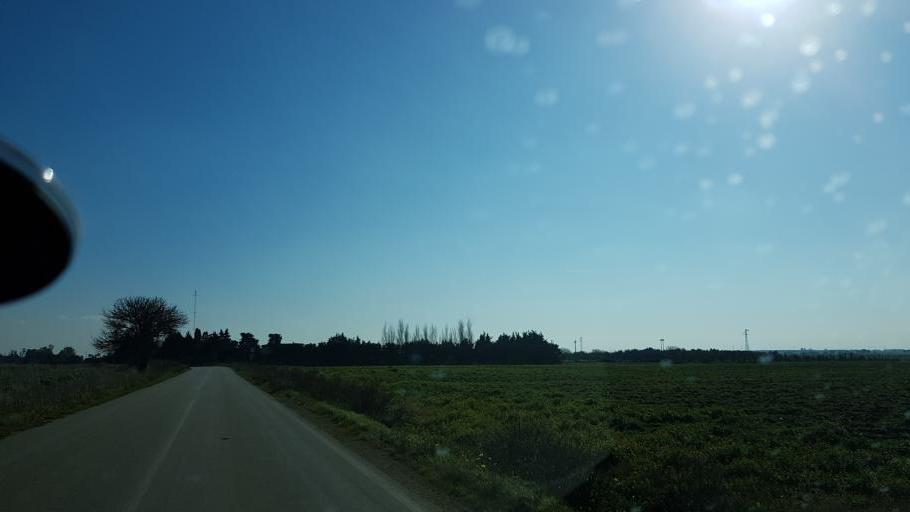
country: IT
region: Apulia
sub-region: Provincia di Brindisi
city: Brindisi
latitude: 40.6458
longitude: 17.8645
